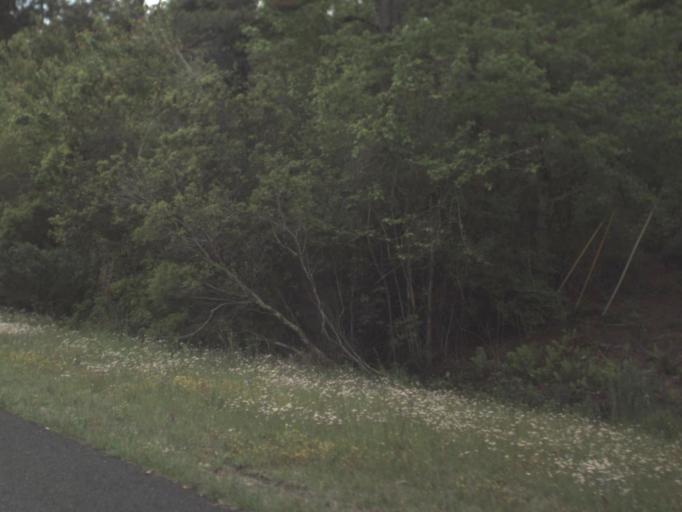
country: US
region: Florida
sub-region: Escambia County
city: Molino
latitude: 30.8205
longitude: -87.3344
